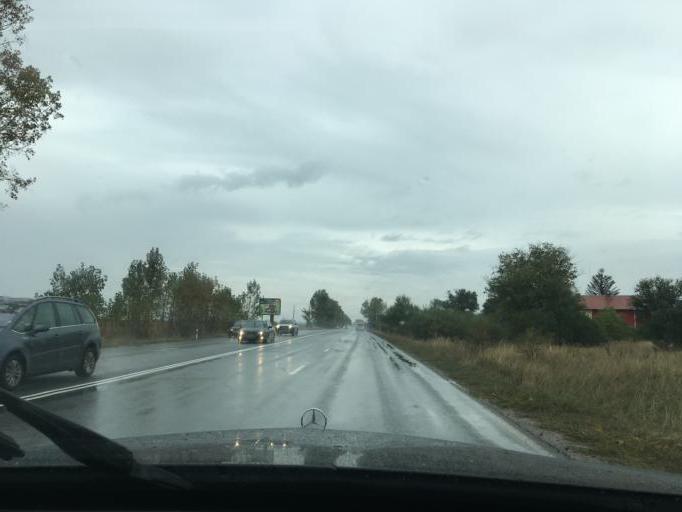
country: BG
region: Sofiya
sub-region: Obshtina Bozhurishte
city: Bozhurishte
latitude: 42.7751
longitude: 23.1838
